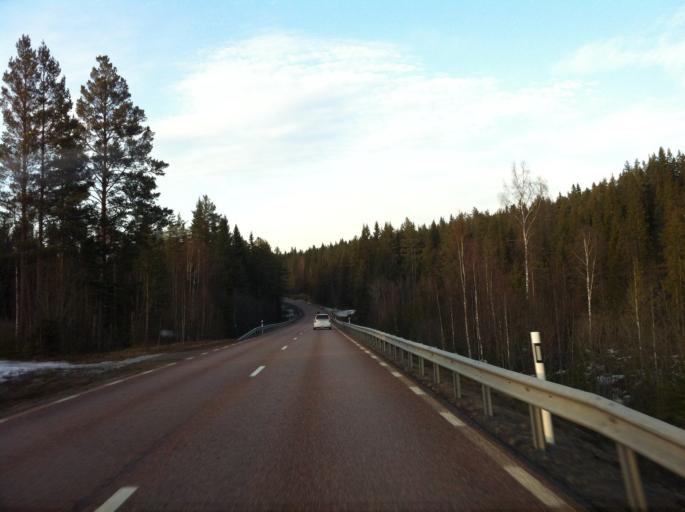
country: SE
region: Dalarna
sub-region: Vansbro Kommun
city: Vansbro
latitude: 60.4162
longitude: 14.2319
